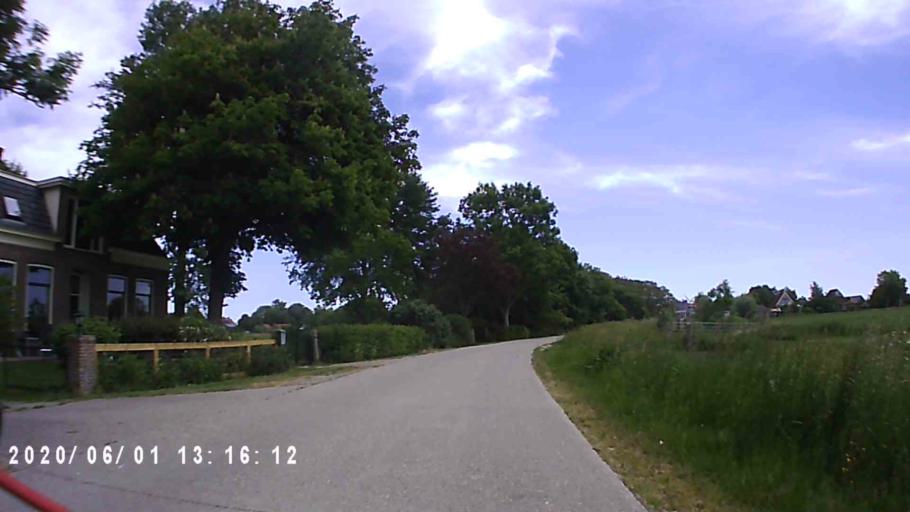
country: NL
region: Friesland
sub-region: Gemeente Littenseradiel
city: Wommels
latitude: 53.1198
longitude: 5.5656
